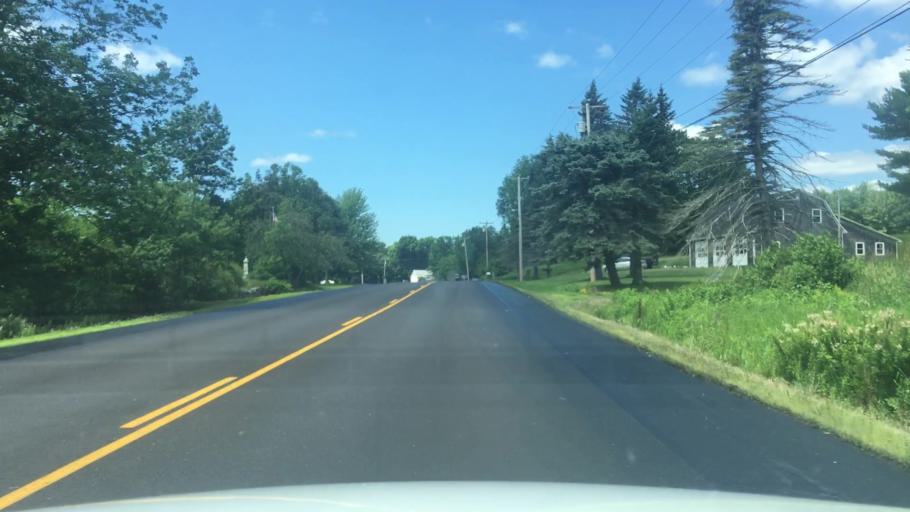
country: US
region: Maine
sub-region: Waldo County
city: Searsmont
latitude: 44.4085
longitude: -69.2125
